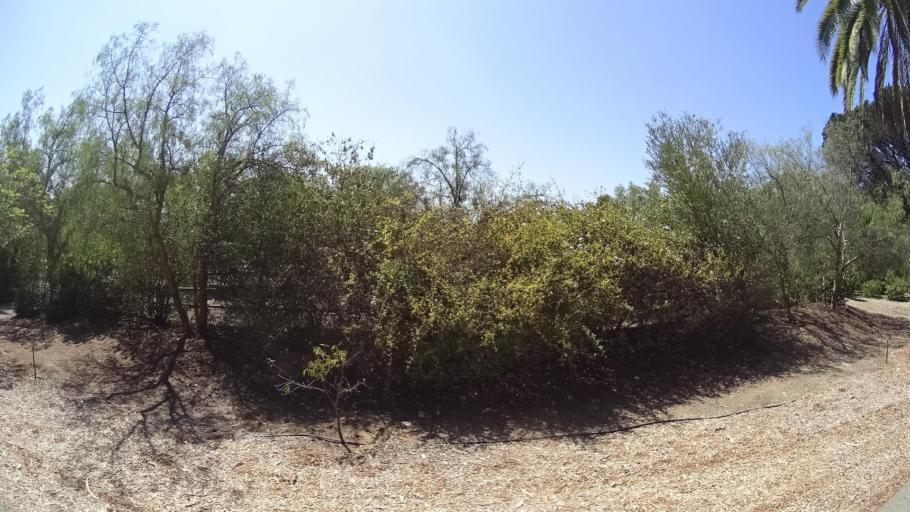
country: US
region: California
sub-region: San Diego County
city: Rancho Santa Fe
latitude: 33.0207
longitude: -117.1832
